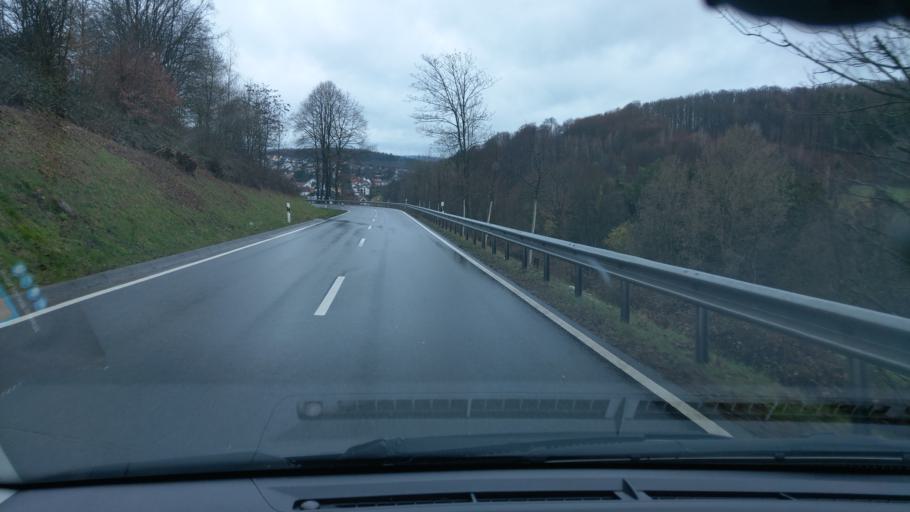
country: DE
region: Rheinland-Pfalz
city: Kashofen
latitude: 49.3468
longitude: 7.4184
